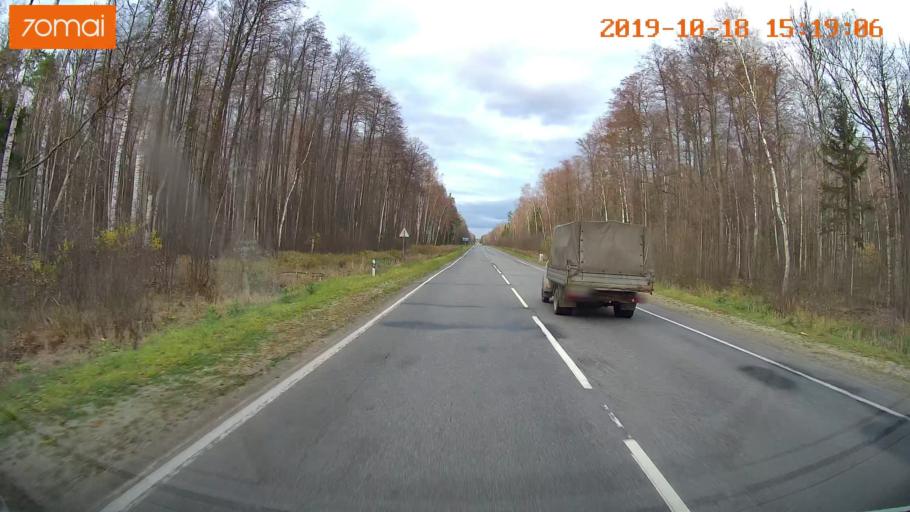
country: RU
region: Vladimir
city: Anopino
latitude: 55.6682
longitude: 40.7351
